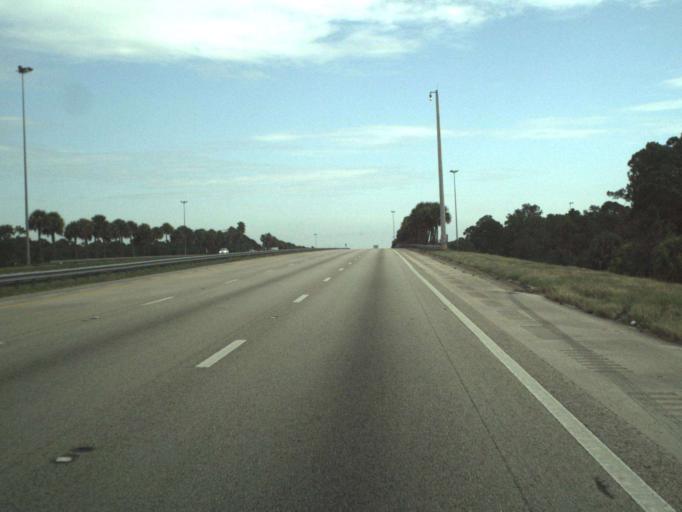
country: US
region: Florida
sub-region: Saint Lucie County
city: Port Saint Lucie
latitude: 27.2610
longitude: -80.4206
